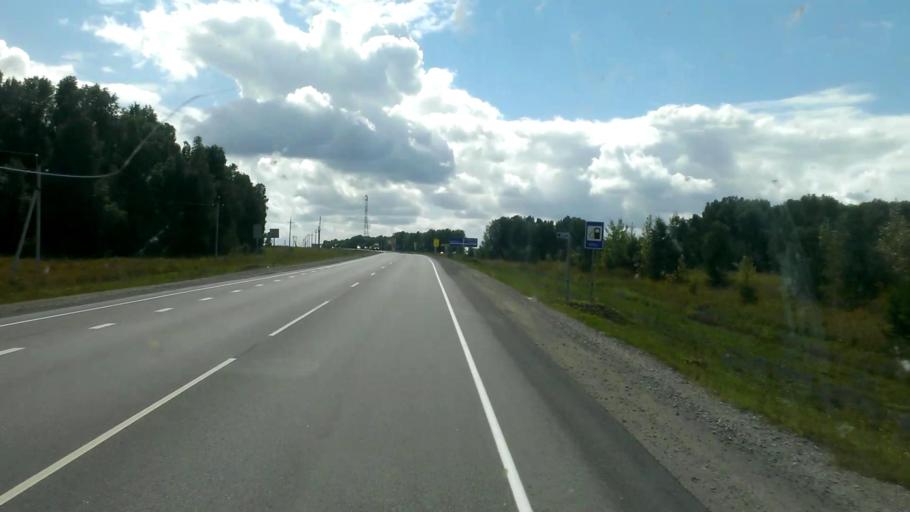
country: RU
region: Altai Krai
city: Troitskoye
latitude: 52.9725
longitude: 84.7478
